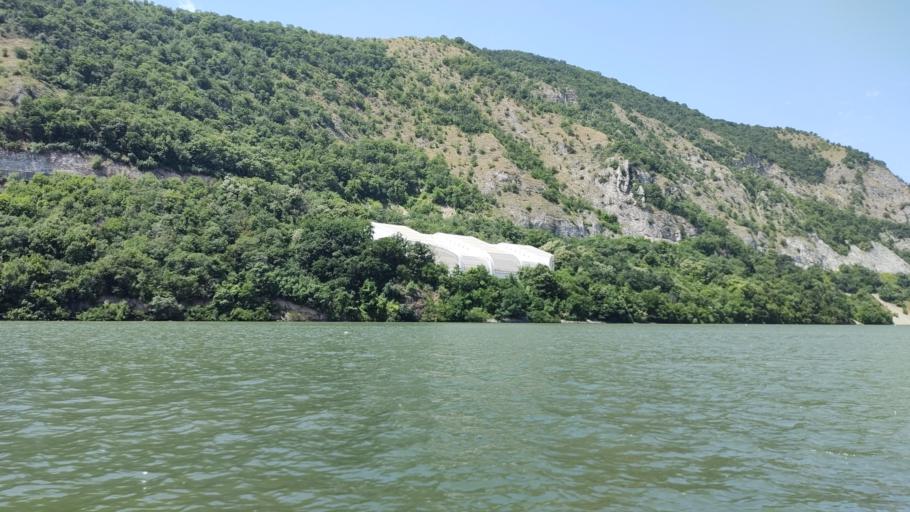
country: RO
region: Mehedinti
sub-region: Comuna Svinita
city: Svinita
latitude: 44.5560
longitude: 22.0299
